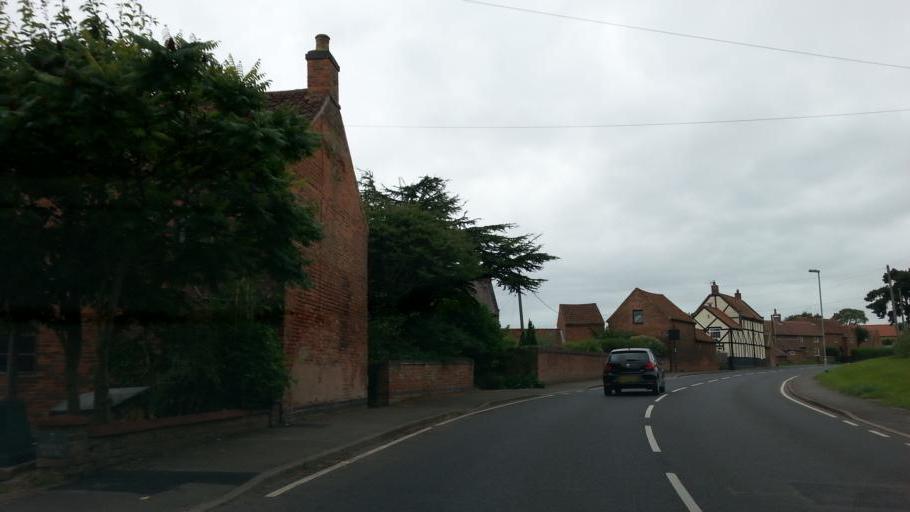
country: GB
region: England
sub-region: Nottinghamshire
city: Farndon
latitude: 53.0821
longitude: -0.8965
